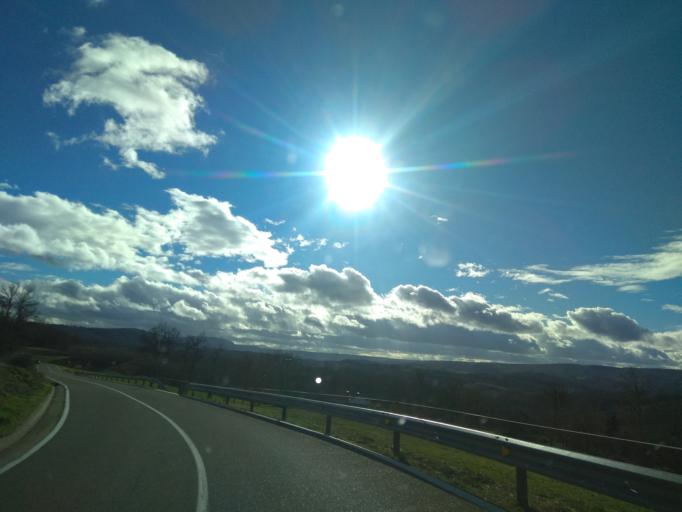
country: ES
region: Cantabria
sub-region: Provincia de Cantabria
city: San Martin de Elines
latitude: 42.9155
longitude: -3.8676
